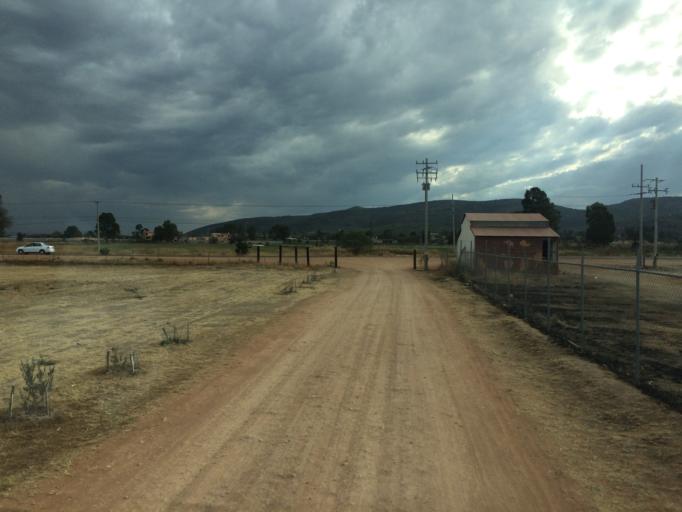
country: MX
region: Queretaro
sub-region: Tequisquiapan
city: Tequisquiapan
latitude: 20.5445
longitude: -99.9535
